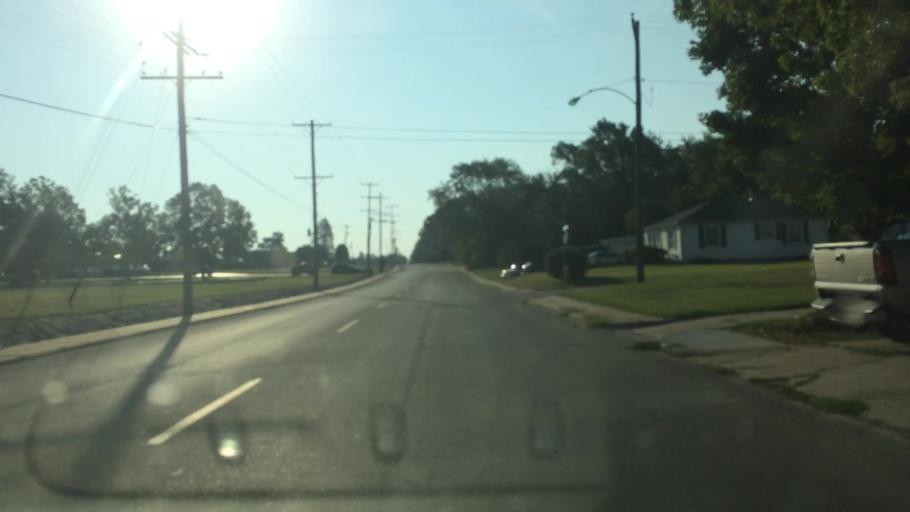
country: US
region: Missouri
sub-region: Greene County
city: Springfield
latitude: 37.2184
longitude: -93.2682
